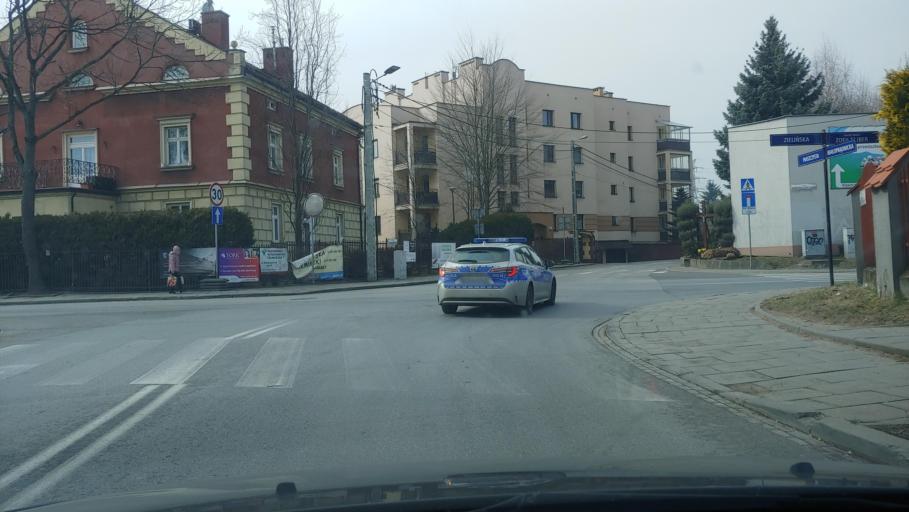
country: PL
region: Lesser Poland Voivodeship
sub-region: Powiat krakowski
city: Zielonki
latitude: 50.0967
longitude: 19.9330
